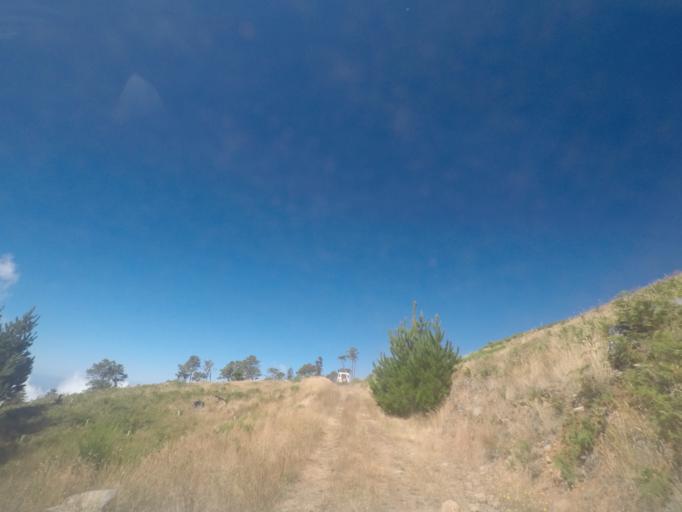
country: PT
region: Madeira
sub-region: Funchal
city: Nossa Senhora do Monte
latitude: 32.7090
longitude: -16.9080
